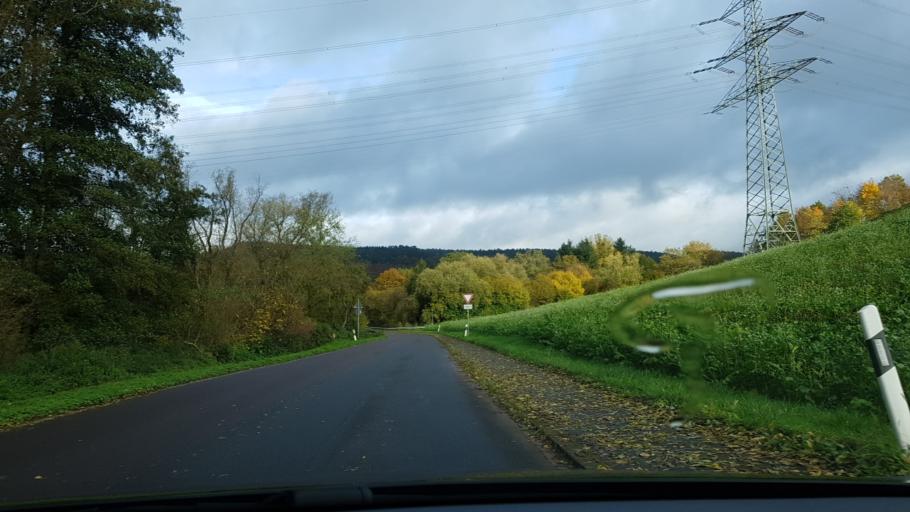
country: DE
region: Rheinland-Pfalz
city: Schweich
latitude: 49.8316
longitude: 6.7357
